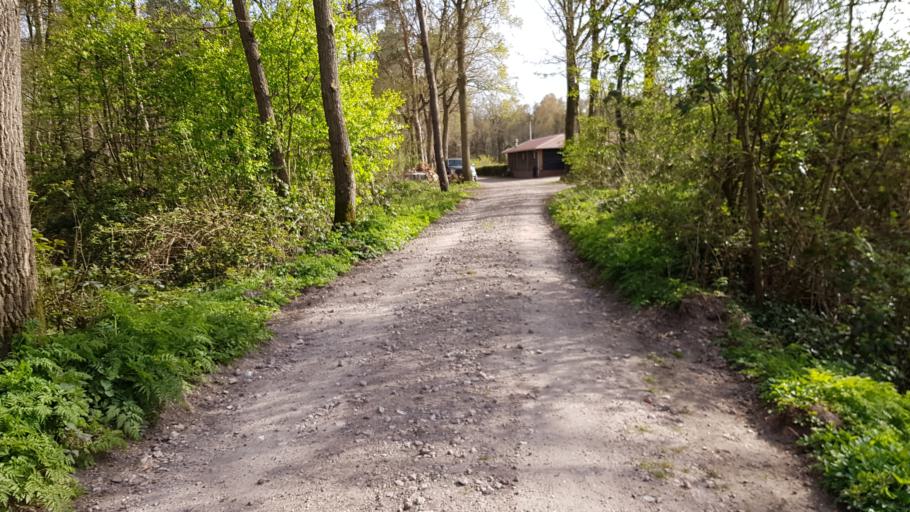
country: NL
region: Gelderland
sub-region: Gemeente Barneveld
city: Terschuur
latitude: 52.1825
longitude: 5.5476
